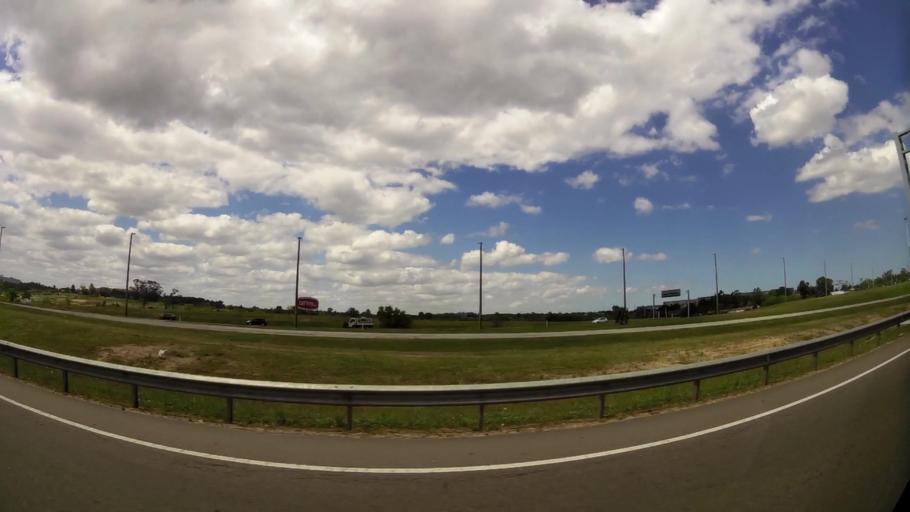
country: UY
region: Canelones
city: La Paz
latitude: -34.8203
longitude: -56.2557
